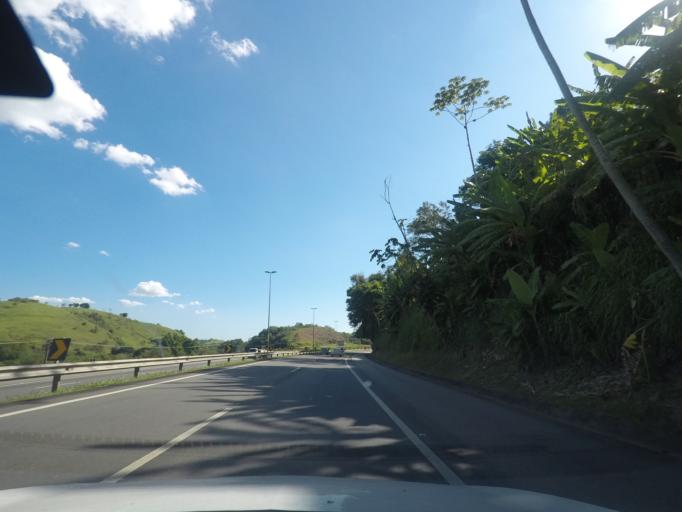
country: BR
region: Rio de Janeiro
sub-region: Guapimirim
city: Guapimirim
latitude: -22.6229
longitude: -43.0442
